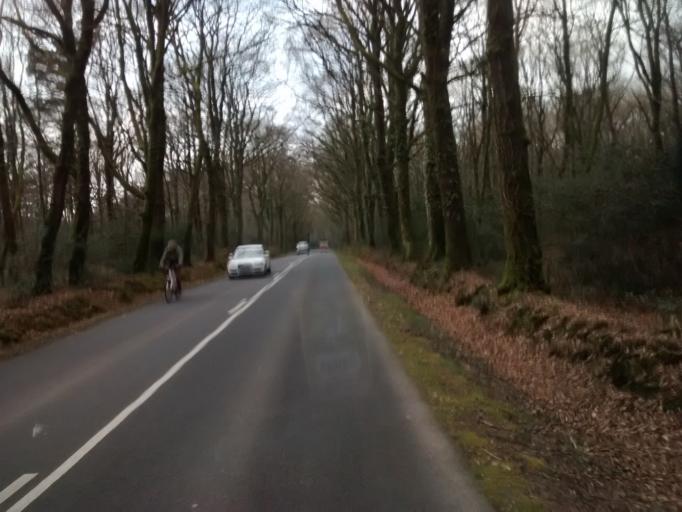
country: FR
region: Brittany
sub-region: Departement d'Ille-et-Vilaine
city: Paimpont
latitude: 48.0191
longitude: -2.1604
